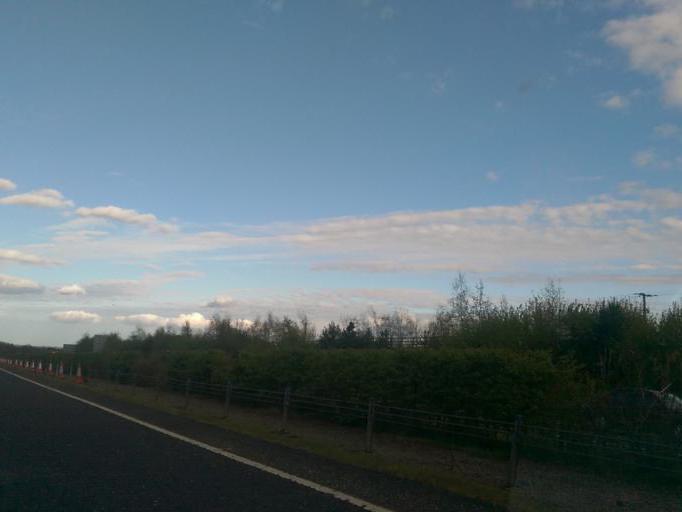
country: IE
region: Leinster
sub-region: Kildare
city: Kilcock
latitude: 53.4097
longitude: -6.7218
